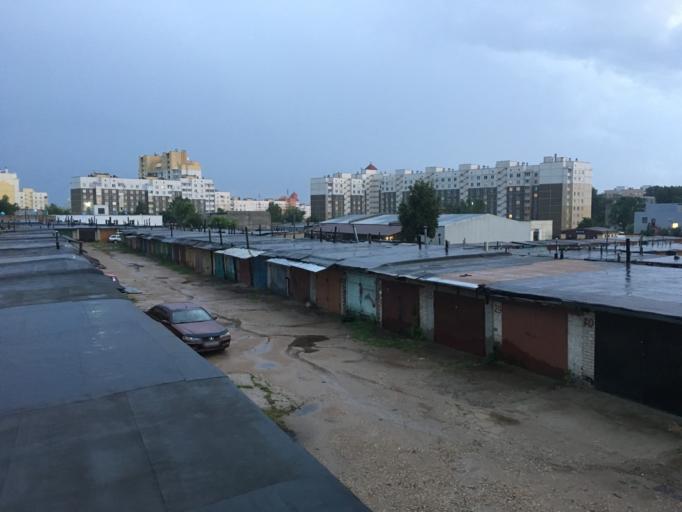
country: BY
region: Grodnenskaya
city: Hrodna
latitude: 53.6994
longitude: 23.8279
